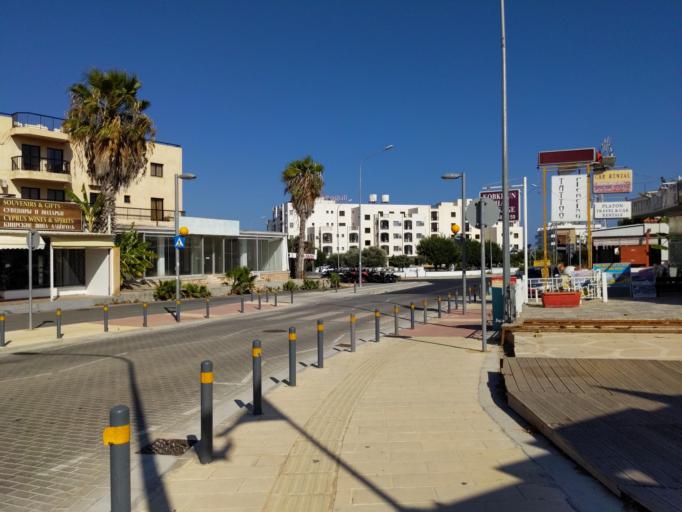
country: CY
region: Ammochostos
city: Protaras
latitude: 35.0308
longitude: 34.0377
